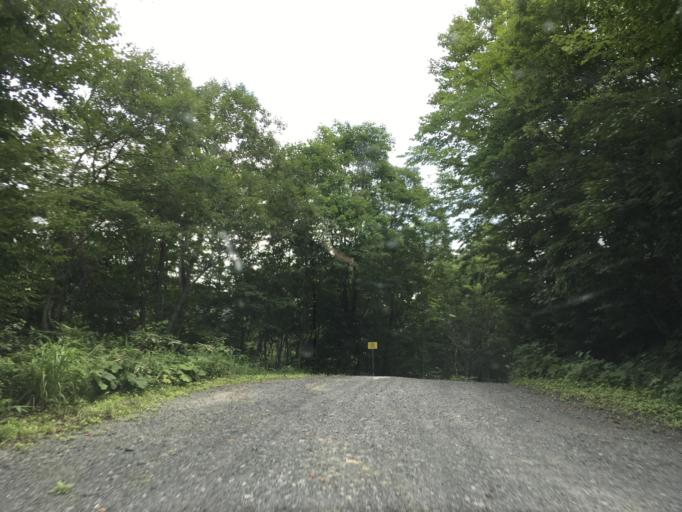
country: JP
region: Iwate
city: Ichinoseki
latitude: 38.9590
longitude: 140.8470
